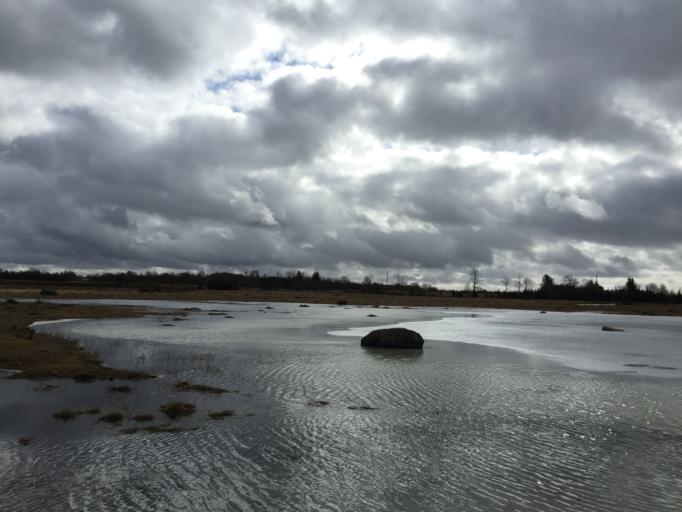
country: EE
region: Laeaene
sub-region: Ridala Parish
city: Uuemoisa
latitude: 58.7274
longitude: 23.6000
